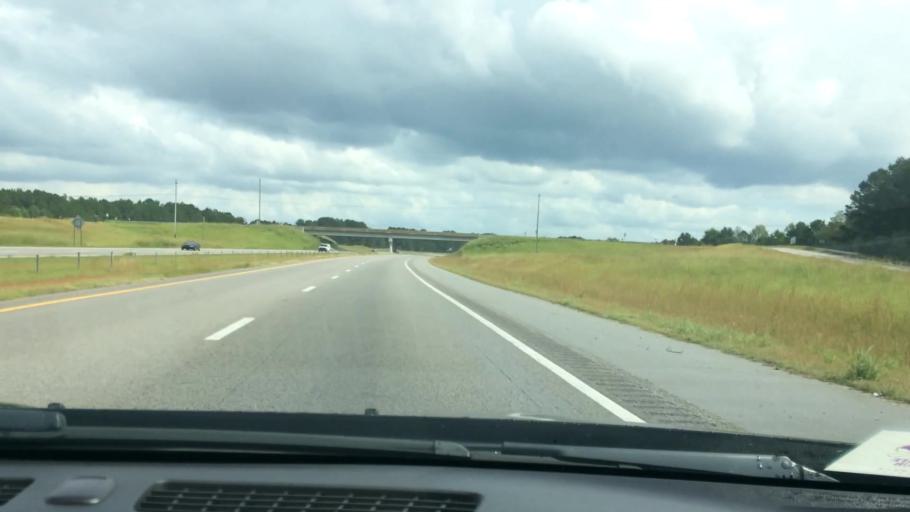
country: US
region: North Carolina
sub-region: Wilson County
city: Wilson
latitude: 35.6715
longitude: -77.8083
